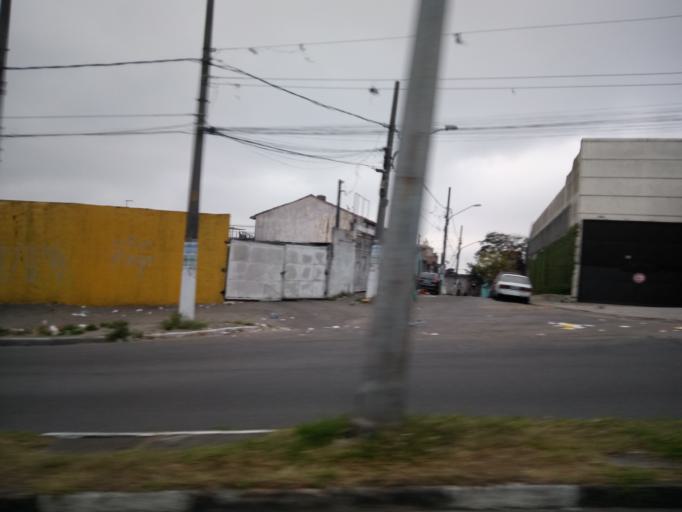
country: BR
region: Sao Paulo
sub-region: Diadema
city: Diadema
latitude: -23.6753
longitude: -46.6302
